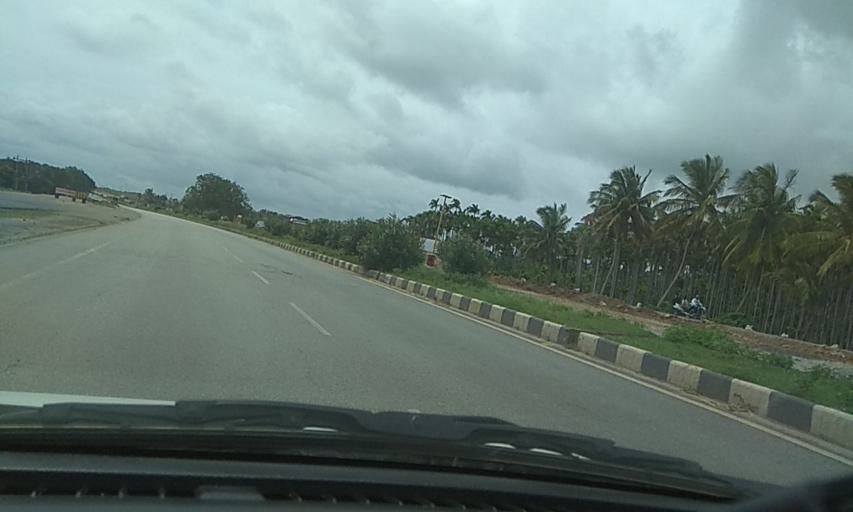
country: IN
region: Karnataka
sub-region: Davanagere
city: Mayakonda
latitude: 14.3412
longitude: 76.2081
